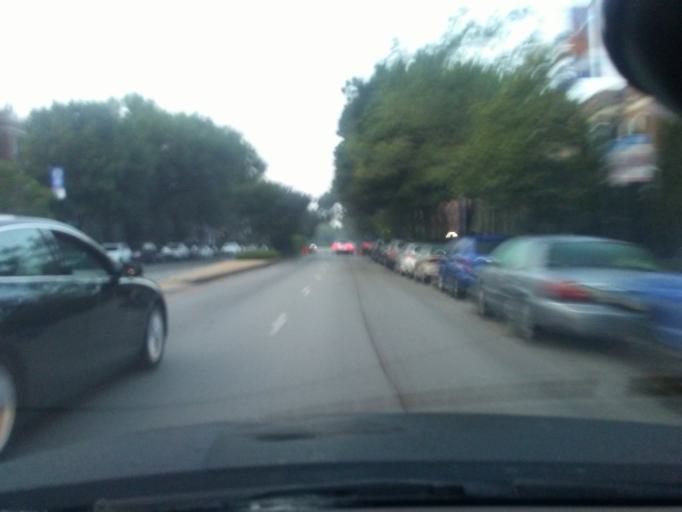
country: US
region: Illinois
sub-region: Cook County
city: Lincolnwood
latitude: 41.9612
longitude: -87.6693
